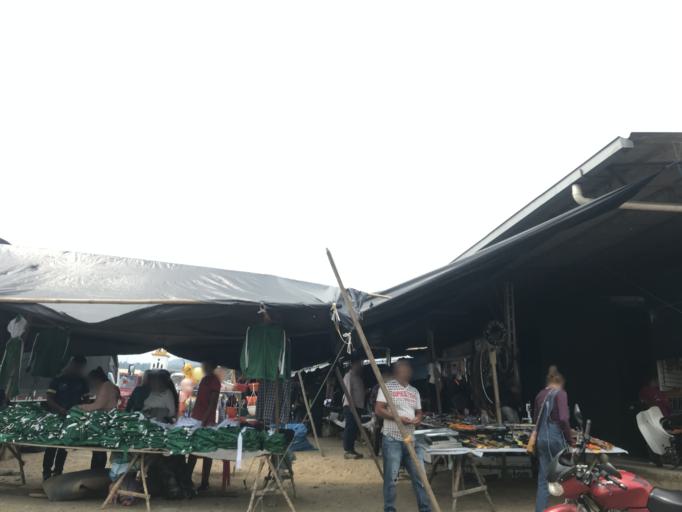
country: CO
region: Huila
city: San Agustin
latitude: 1.8801
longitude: -76.2706
